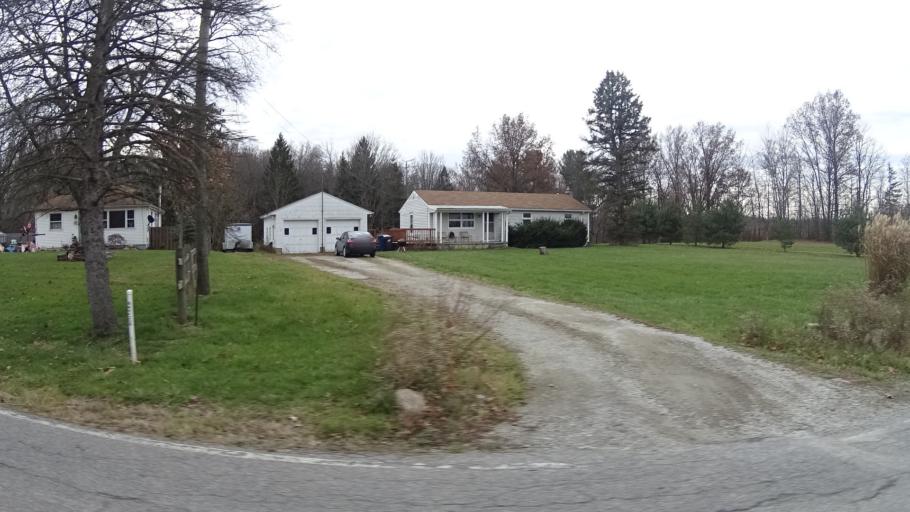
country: US
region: Ohio
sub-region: Cuyahoga County
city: Berea
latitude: 41.3311
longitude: -81.8857
